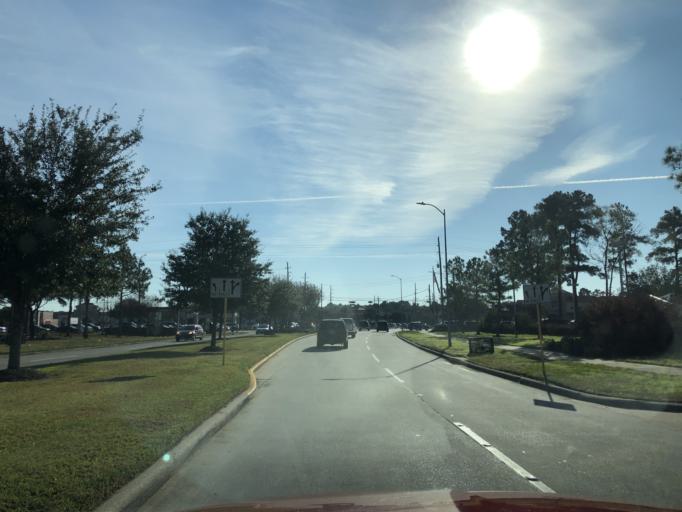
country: US
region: Texas
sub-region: Harris County
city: Tomball
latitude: 30.0337
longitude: -95.5565
